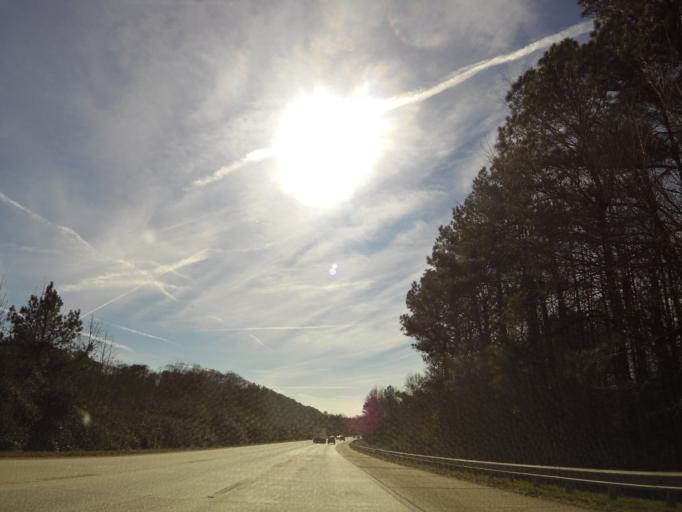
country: US
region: Georgia
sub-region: Troup County
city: Hogansville
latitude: 33.0766
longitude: -84.9242
